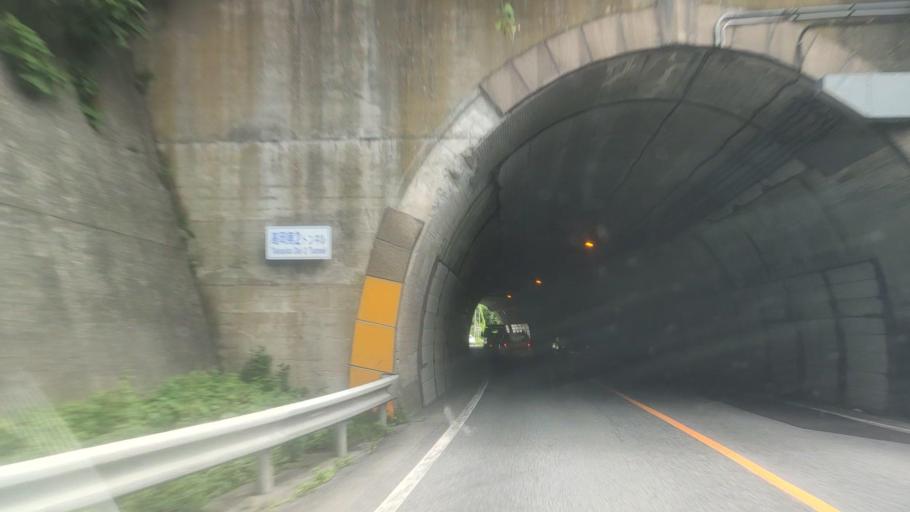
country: JP
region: Hokkaido
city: Niseko Town
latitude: 42.5889
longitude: 140.6779
